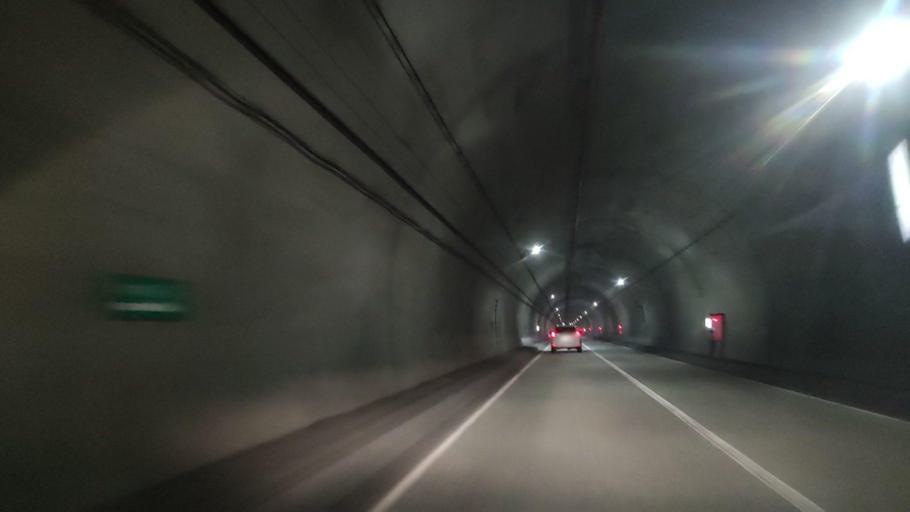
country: JP
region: Hokkaido
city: Rumoi
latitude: 43.7154
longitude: 141.3299
